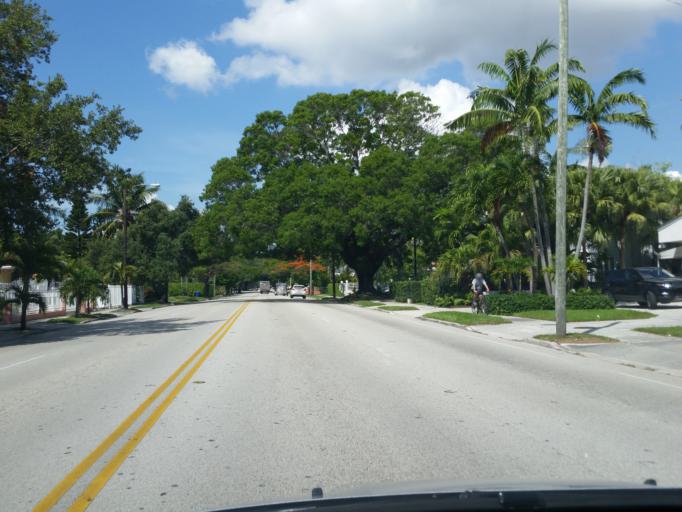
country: US
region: Florida
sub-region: Miami-Dade County
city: Miami
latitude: 25.7494
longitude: -80.2076
